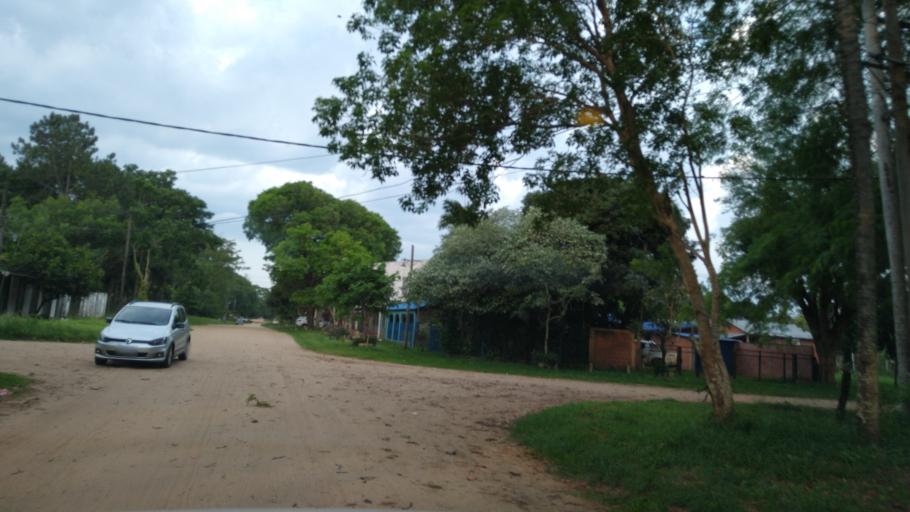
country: AR
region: Corrientes
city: Ituzaingo
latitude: -27.5921
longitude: -56.7059
